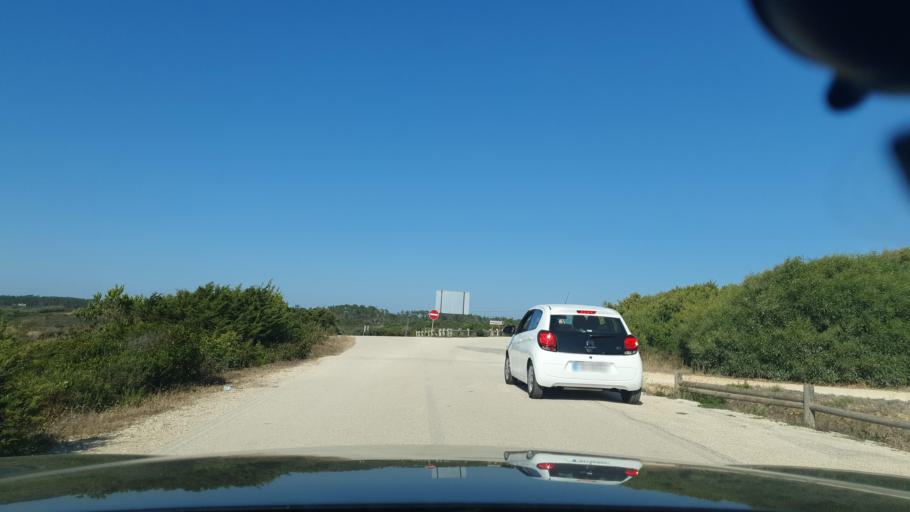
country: PT
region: Beja
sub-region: Odemira
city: Sao Teotonio
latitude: 37.4381
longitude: -8.7981
